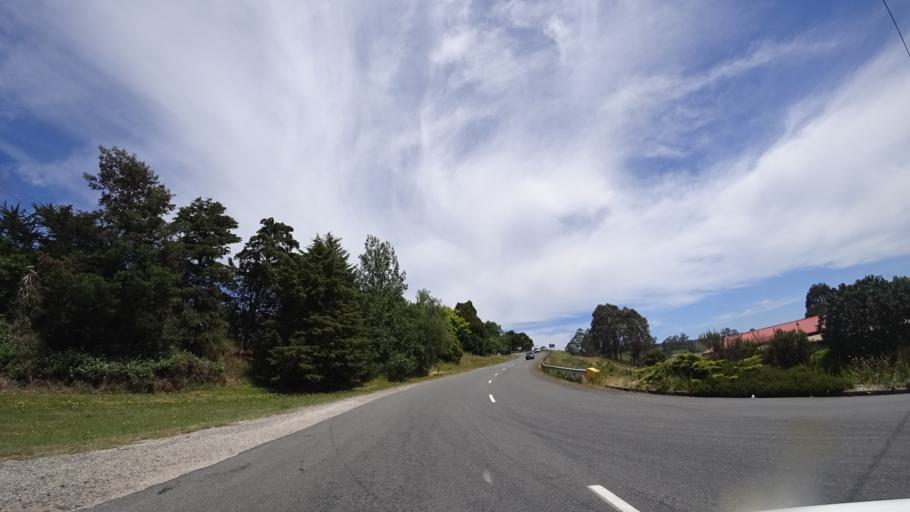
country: AU
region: Tasmania
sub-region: Dorset
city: Scottsdale
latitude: -41.1697
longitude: 147.7370
